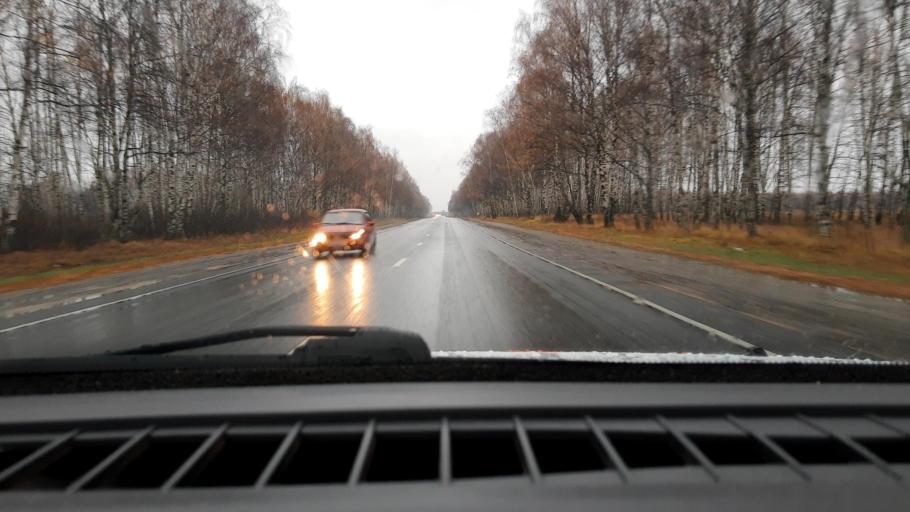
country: RU
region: Nizjnij Novgorod
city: Sitniki
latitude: 56.5148
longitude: 44.0245
